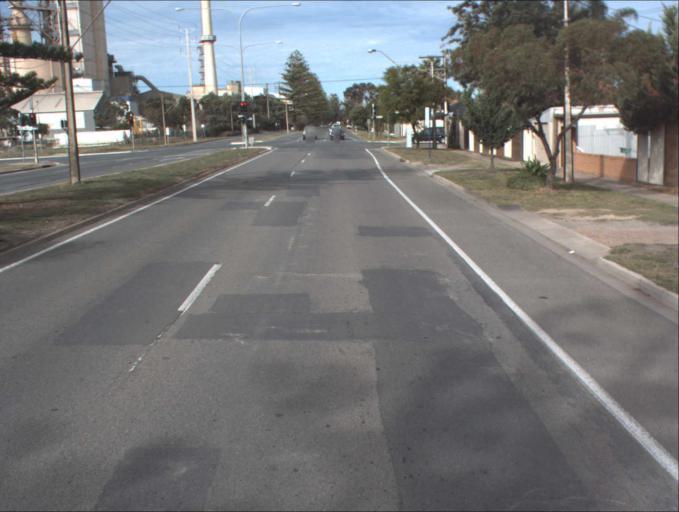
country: AU
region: South Australia
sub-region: Port Adelaide Enfield
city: Birkenhead
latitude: -34.8282
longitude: 138.5006
